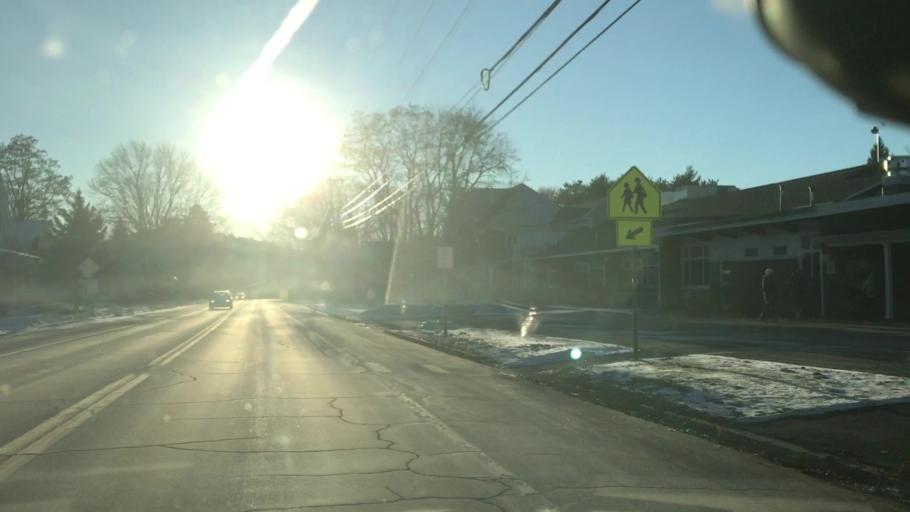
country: US
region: New Hampshire
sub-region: Grafton County
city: Lyme
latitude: 43.8104
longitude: -72.1595
